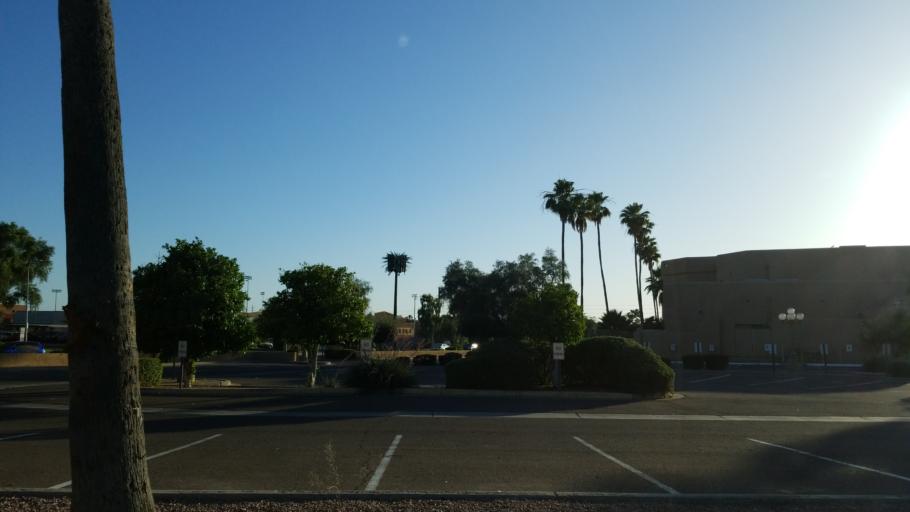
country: US
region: Arizona
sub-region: Maricopa County
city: Scottsdale
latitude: 33.5028
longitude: -111.9057
